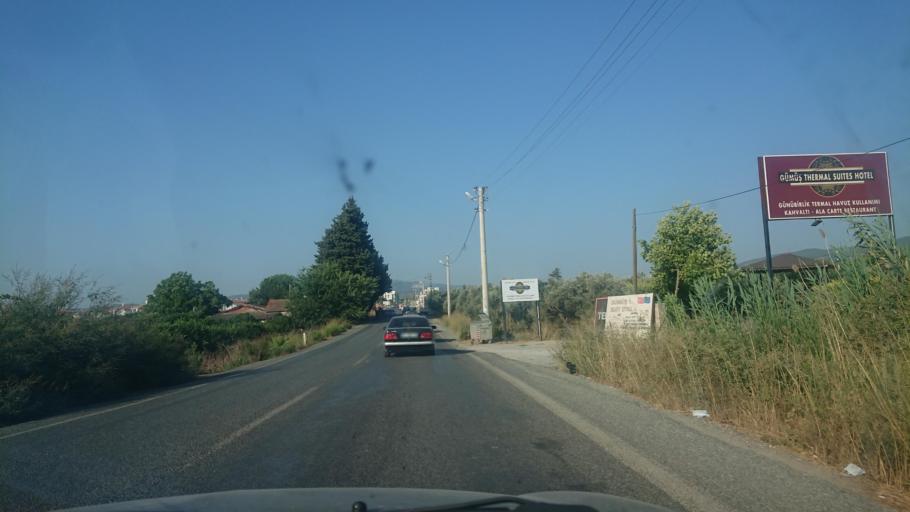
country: TR
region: Aydin
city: Davutlar
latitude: 37.7290
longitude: 27.2685
